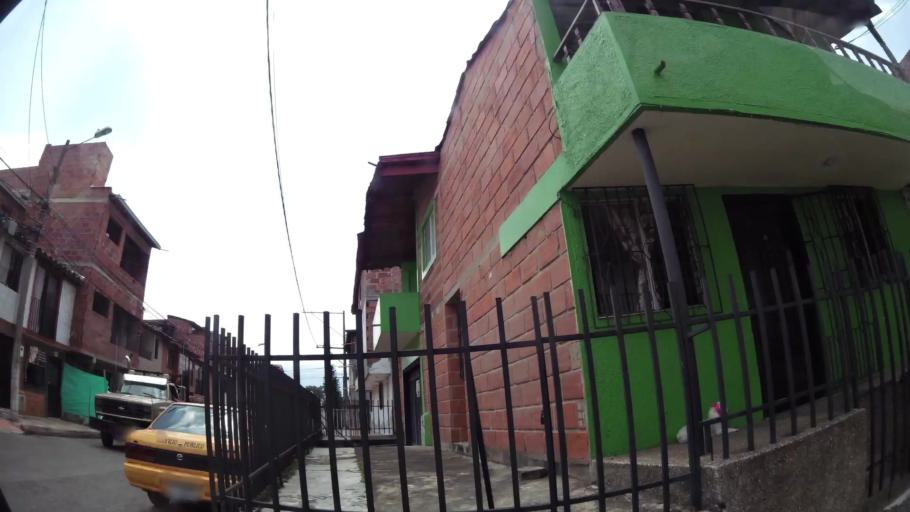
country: CO
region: Antioquia
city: Itagui
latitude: 6.1821
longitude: -75.6065
